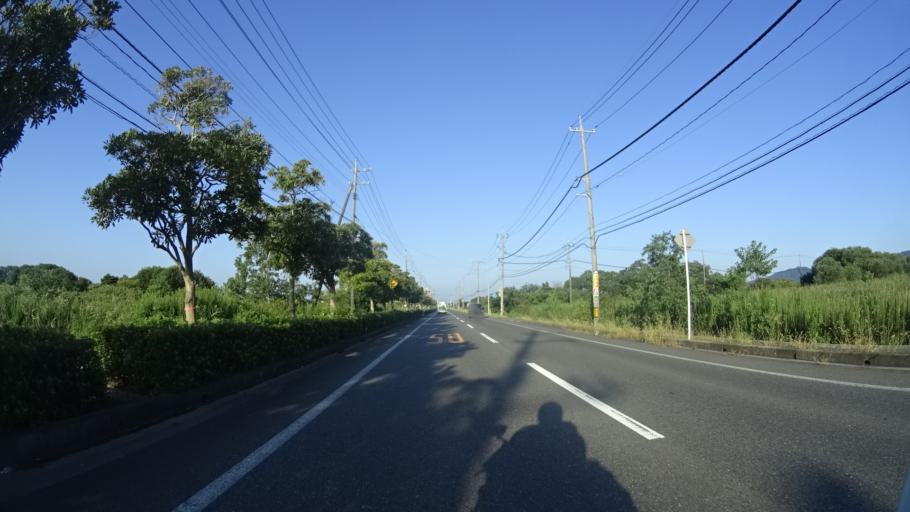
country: JP
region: Shimane
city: Sakaiminato
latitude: 35.5212
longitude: 133.2281
